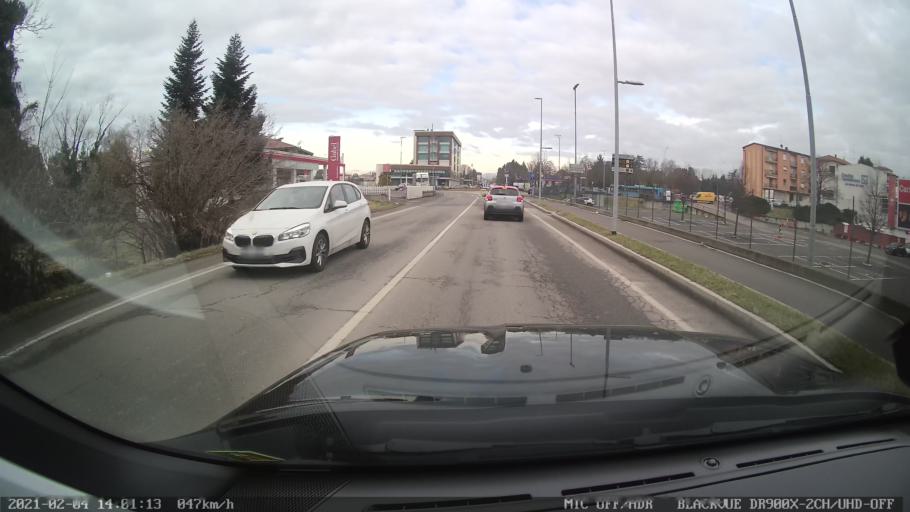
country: IT
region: Lombardy
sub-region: Provincia di Varese
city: Tradate
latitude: 45.7082
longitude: 8.9020
